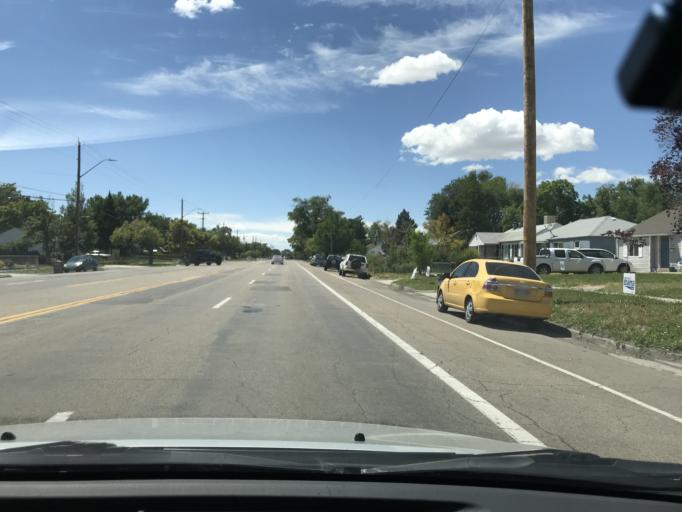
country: US
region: Utah
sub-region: Salt Lake County
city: Salt Lake City
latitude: 40.7825
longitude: -111.9203
